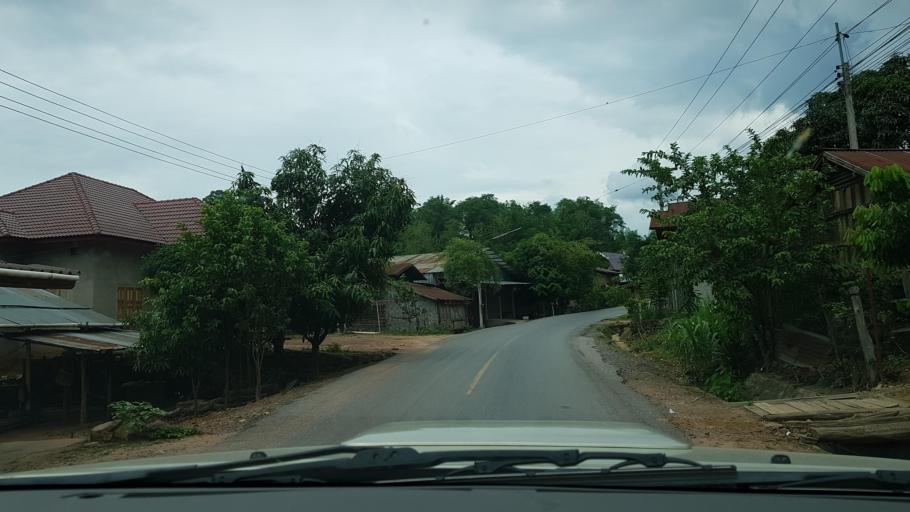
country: LA
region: Loungnamtha
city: Muang Nale
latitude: 20.3543
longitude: 101.6859
